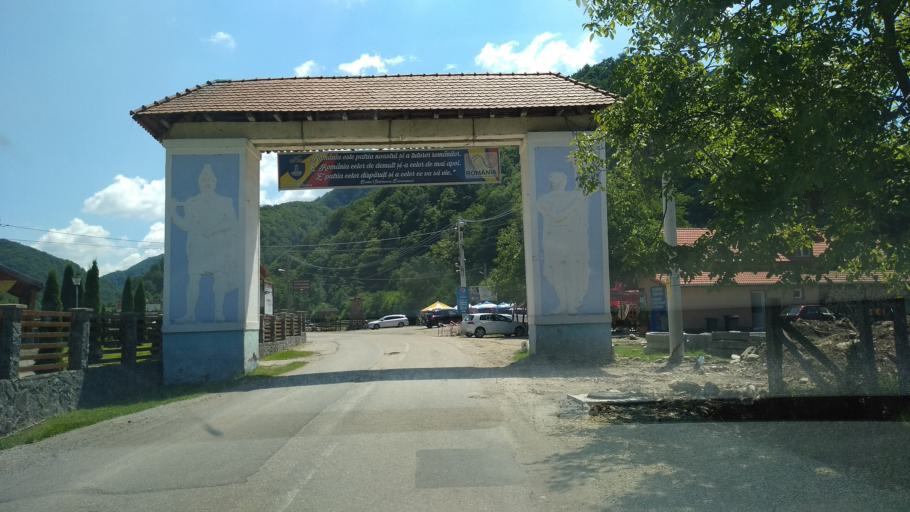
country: RO
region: Hunedoara
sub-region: Comuna Orastioara de Sus
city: Orastioara de Sus
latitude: 45.6806
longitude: 23.1618
